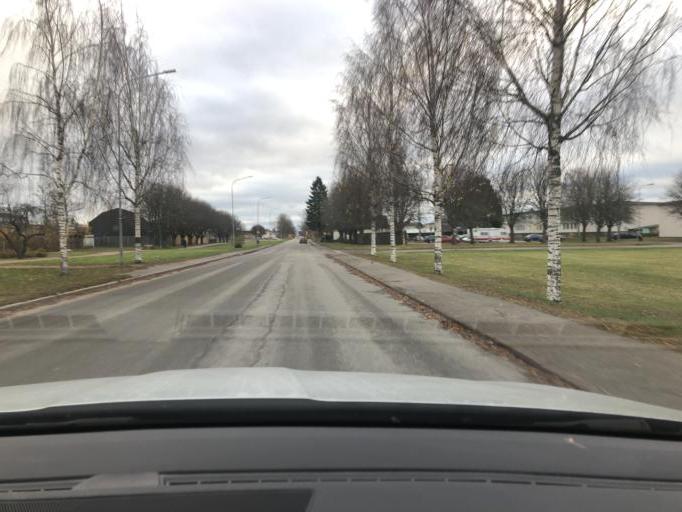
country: SE
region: Uppsala
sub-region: Tierps Kommun
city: Tierp
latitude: 60.3476
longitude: 17.4996
